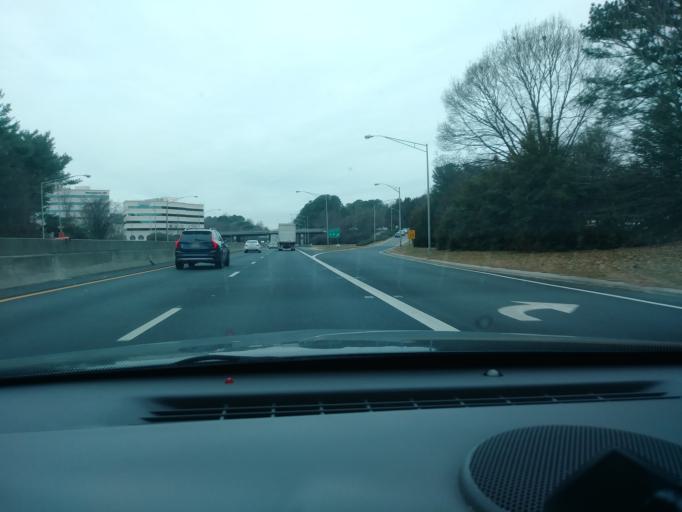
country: US
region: North Carolina
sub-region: Forsyth County
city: Winston-Salem
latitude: 36.0931
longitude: -80.2844
